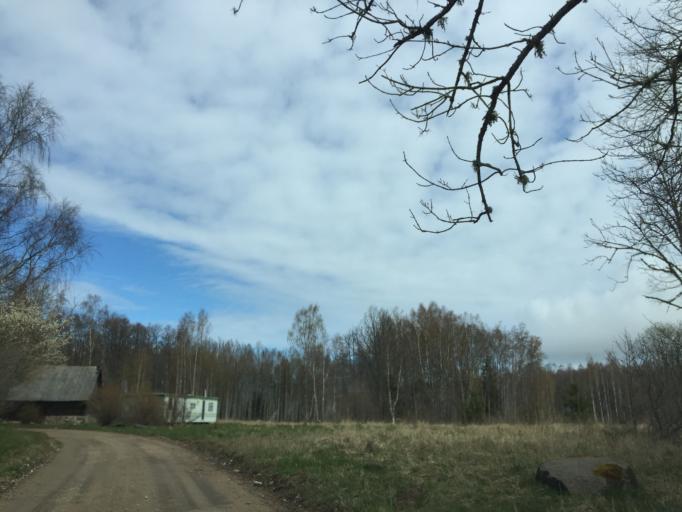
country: LV
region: Salacgrivas
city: Salacgriva
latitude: 57.5388
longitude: 24.3692
